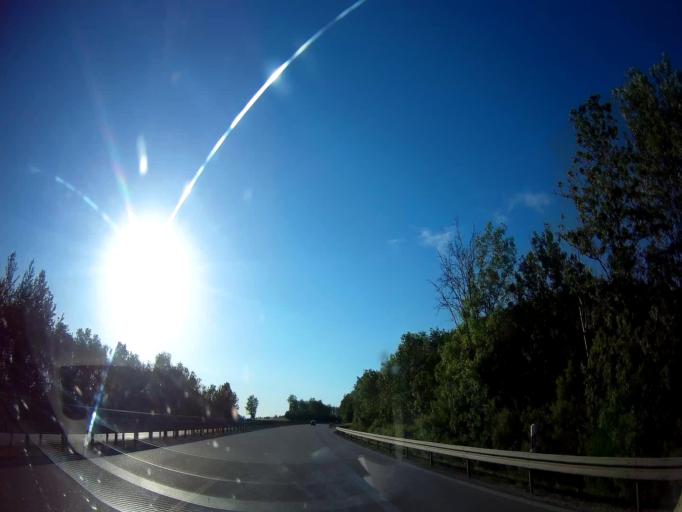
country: DE
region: Bavaria
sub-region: Upper Palatinate
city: Parsberg
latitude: 49.1822
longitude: 11.6879
